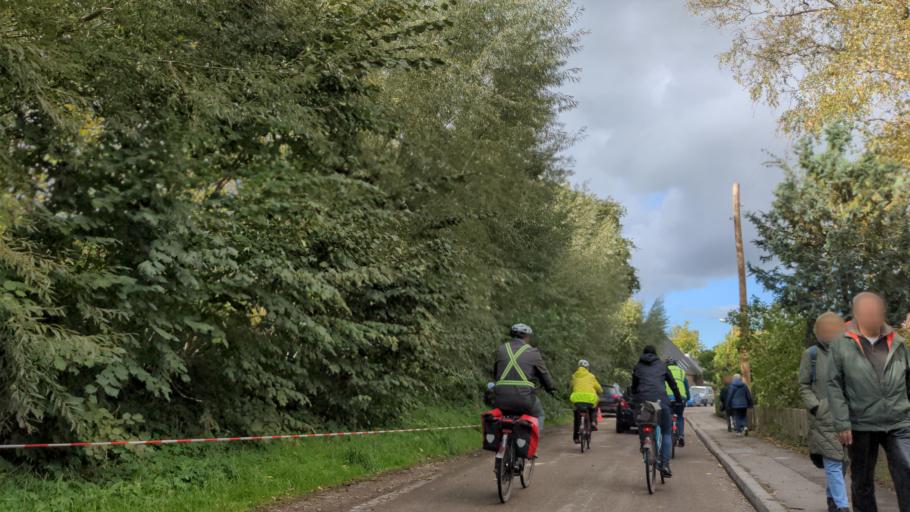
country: DE
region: Schleswig-Holstein
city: Hamberge
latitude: 53.8157
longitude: 10.6178
